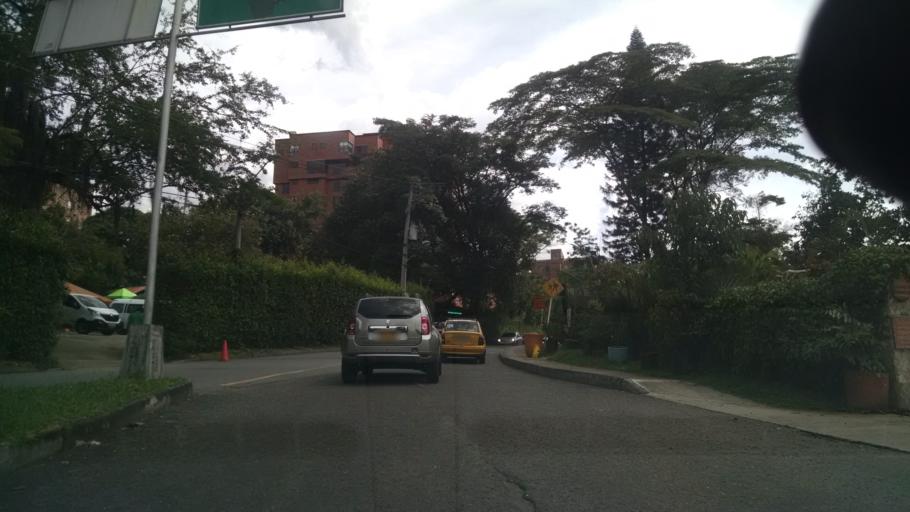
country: CO
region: Antioquia
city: Envigado
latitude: 6.2009
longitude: -75.5662
